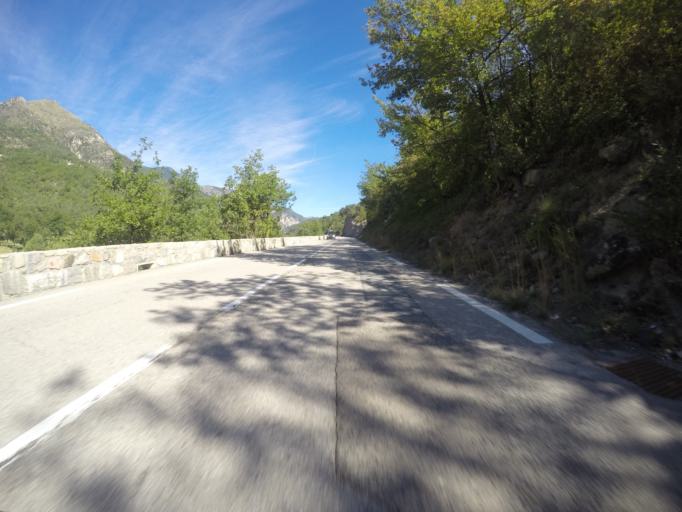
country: FR
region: Provence-Alpes-Cote d'Azur
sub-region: Departement des Alpes-Maritimes
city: Gilette
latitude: 43.9537
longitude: 7.1591
